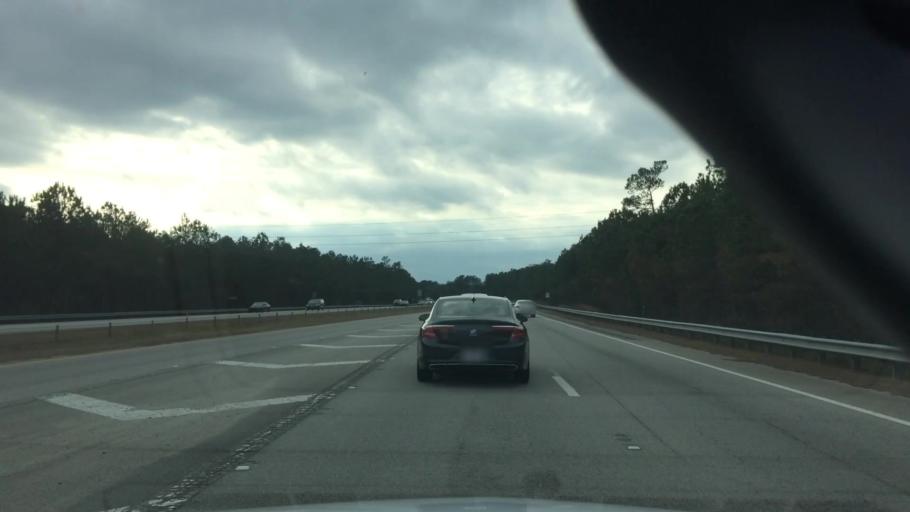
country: US
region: South Carolina
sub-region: Horry County
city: North Myrtle Beach
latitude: 33.8732
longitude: -78.6857
